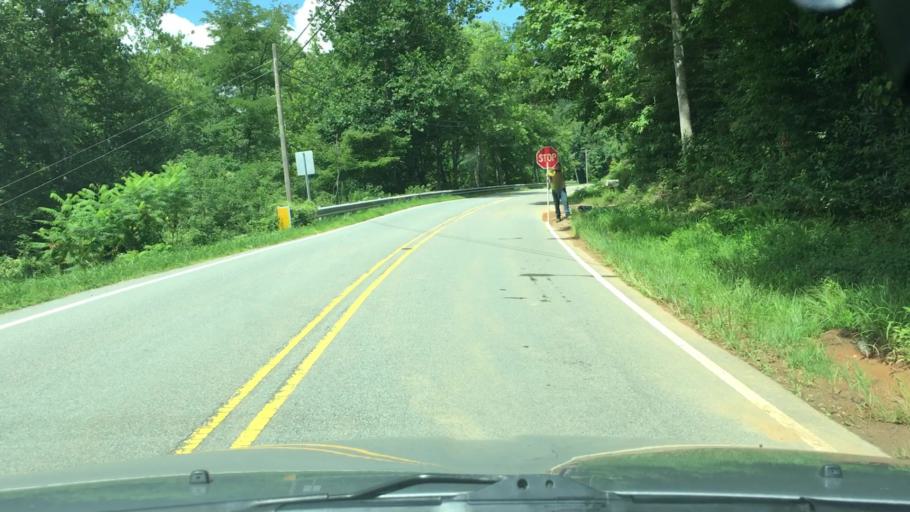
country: US
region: North Carolina
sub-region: Yancey County
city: Burnsville
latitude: 35.7978
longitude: -82.2046
